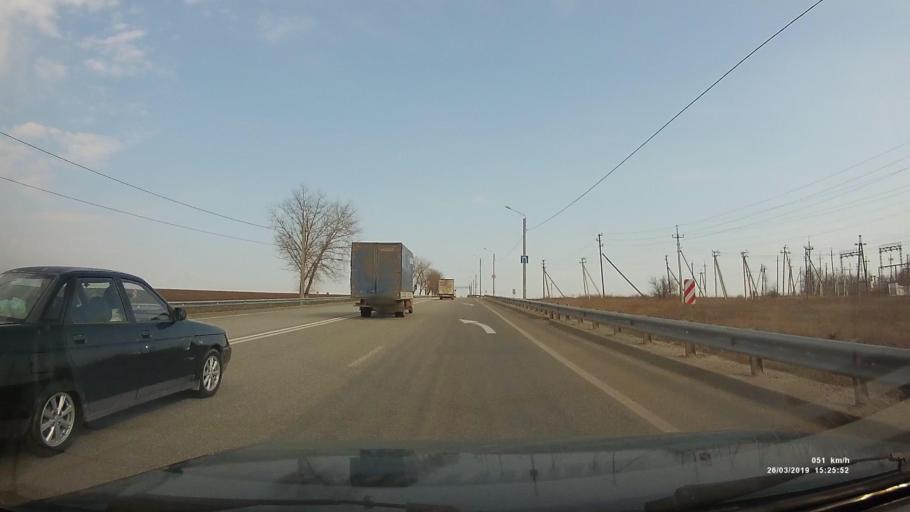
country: RU
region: Rostov
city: Primorka
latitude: 47.3211
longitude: 39.0368
